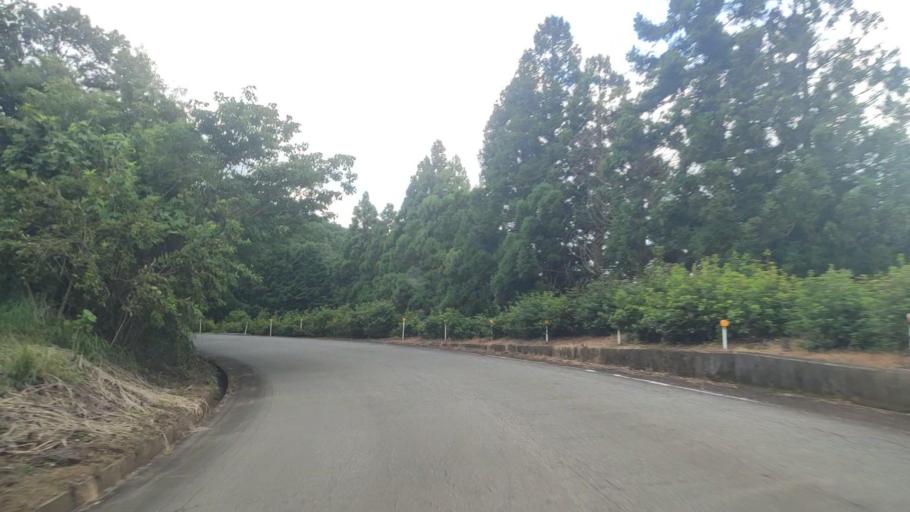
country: JP
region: Kanagawa
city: Hakone
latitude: 35.1285
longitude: 138.9881
